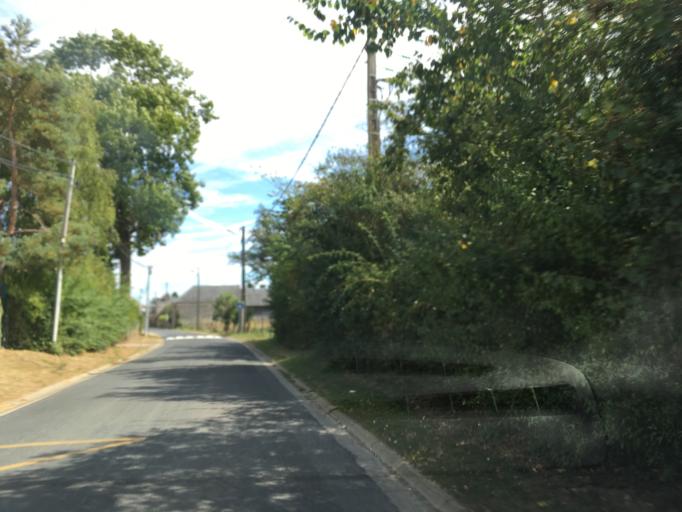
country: FR
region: Haute-Normandie
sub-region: Departement de l'Eure
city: Saint-Aubin-sur-Gaillon
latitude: 49.1358
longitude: 1.2907
